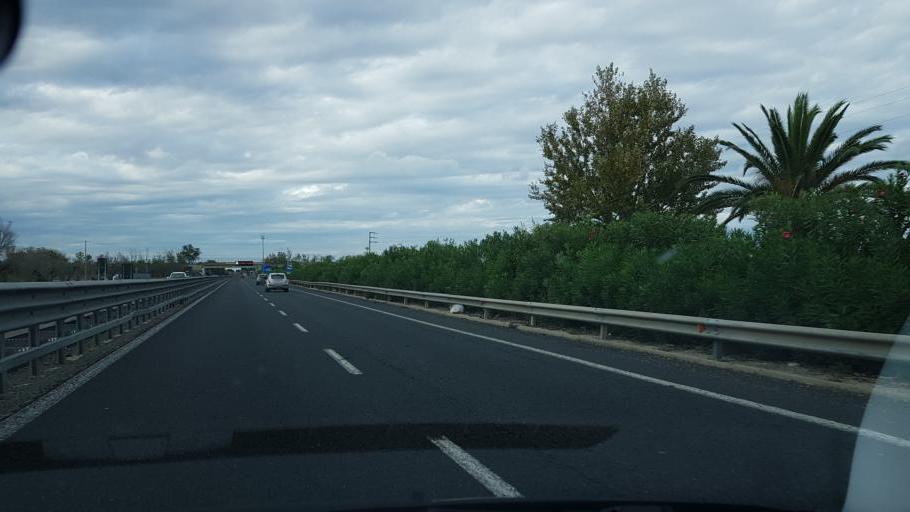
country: IT
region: Apulia
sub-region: Provincia di Lecce
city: Cavallino
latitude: 40.2963
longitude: 18.1952
